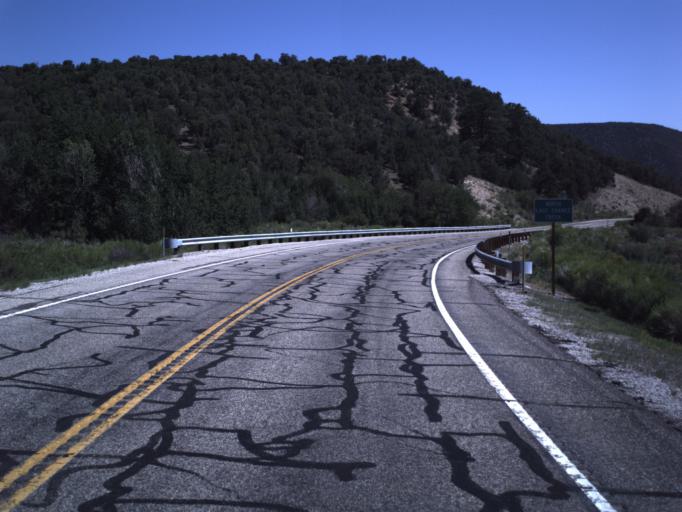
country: US
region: Utah
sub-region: Wayne County
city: Loa
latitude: 38.6565
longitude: -111.4338
